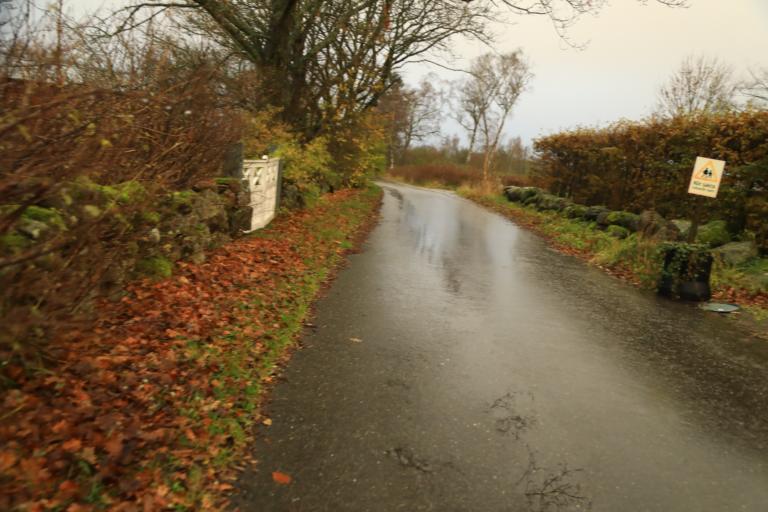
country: SE
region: Halland
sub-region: Varbergs Kommun
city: Traslovslage
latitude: 57.1160
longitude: 12.3089
